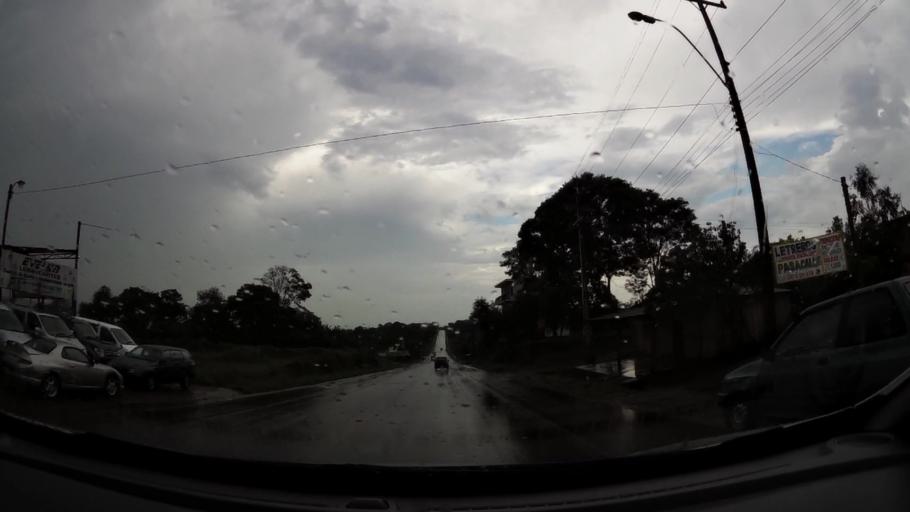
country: PY
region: Alto Parana
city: Presidente Franco
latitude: -25.5615
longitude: -54.6640
